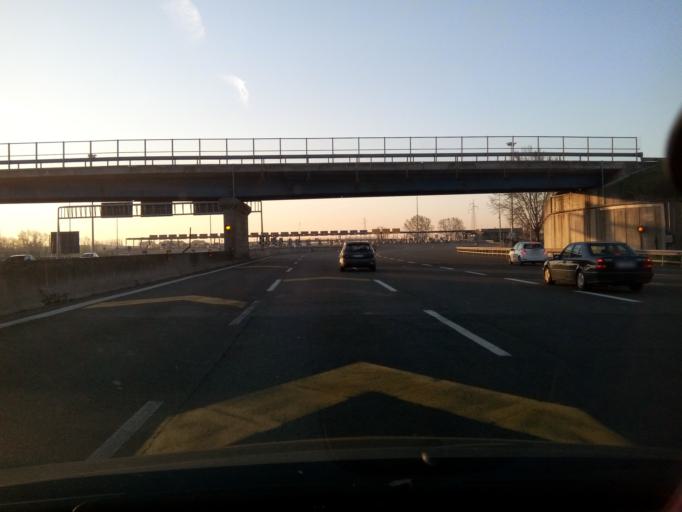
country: IT
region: Lombardy
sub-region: Citta metropolitana di Milano
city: Riozzo
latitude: 45.3515
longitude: 9.3072
